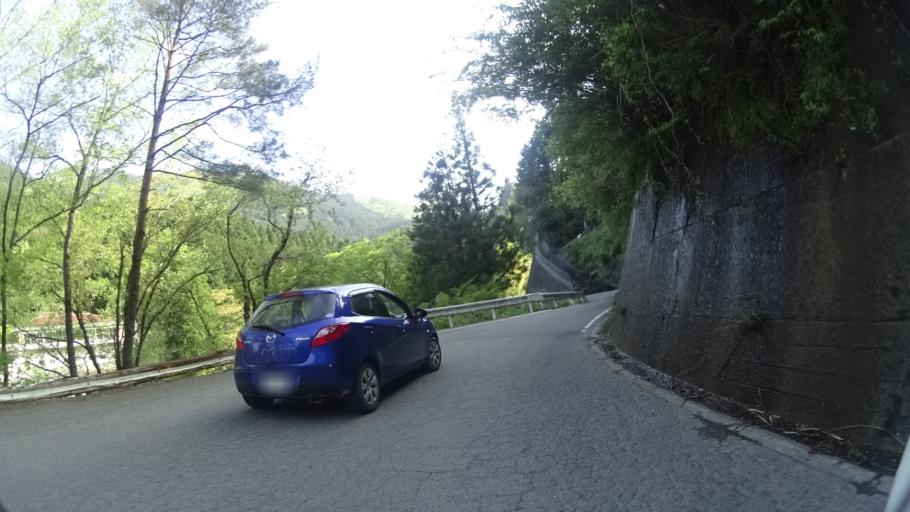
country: JP
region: Tokushima
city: Ikedacho
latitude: 33.8743
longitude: 133.9872
